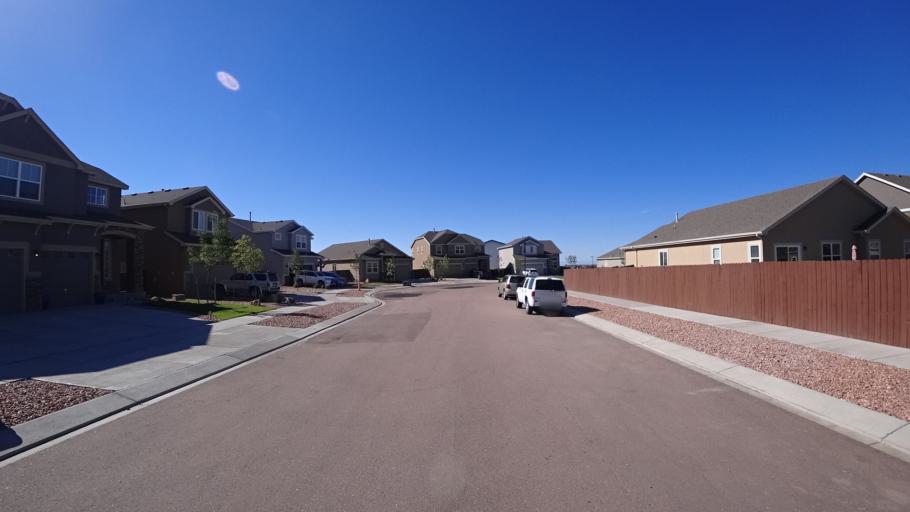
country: US
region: Colorado
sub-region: El Paso County
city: Black Forest
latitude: 38.9452
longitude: -104.6739
